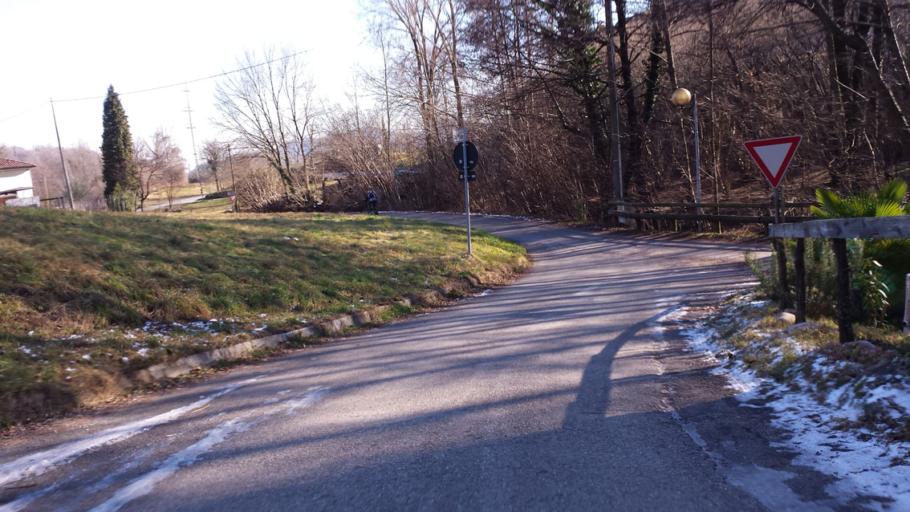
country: IT
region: Veneto
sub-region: Provincia di Treviso
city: Castelcucco
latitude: 45.8346
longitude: 11.8720
